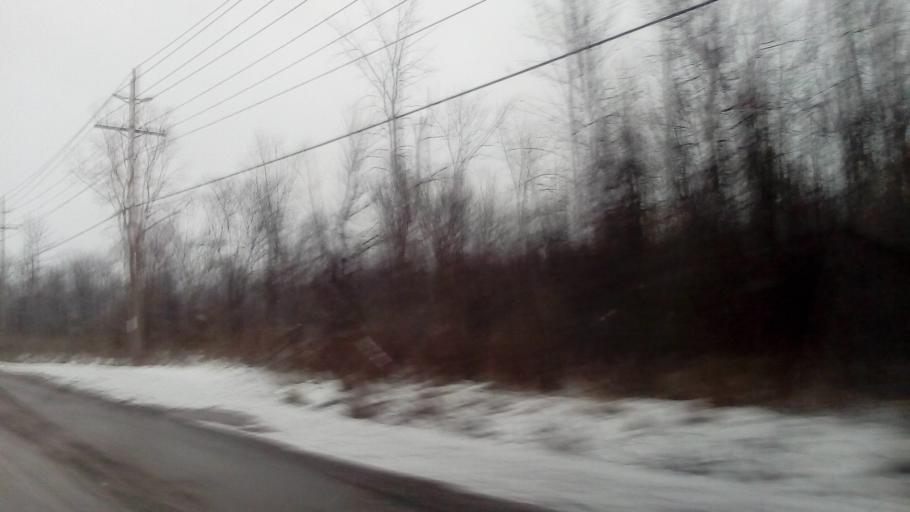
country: CA
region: Ontario
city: Ottawa
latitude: 45.4500
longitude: -75.5766
